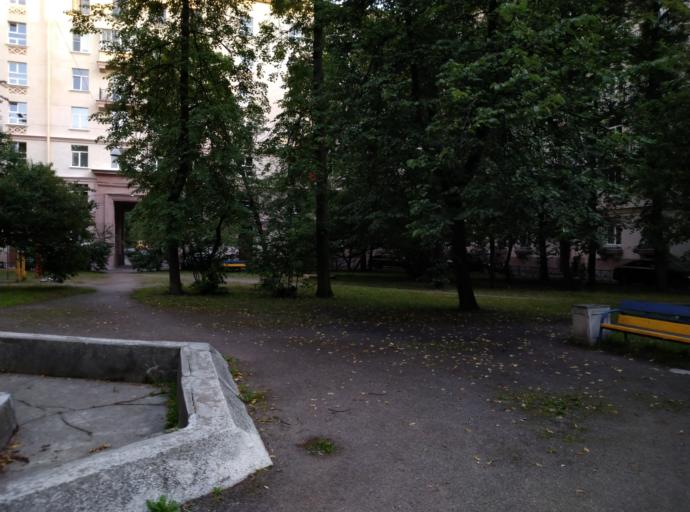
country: RU
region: St.-Petersburg
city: Kupchino
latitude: 59.8613
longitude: 30.3342
